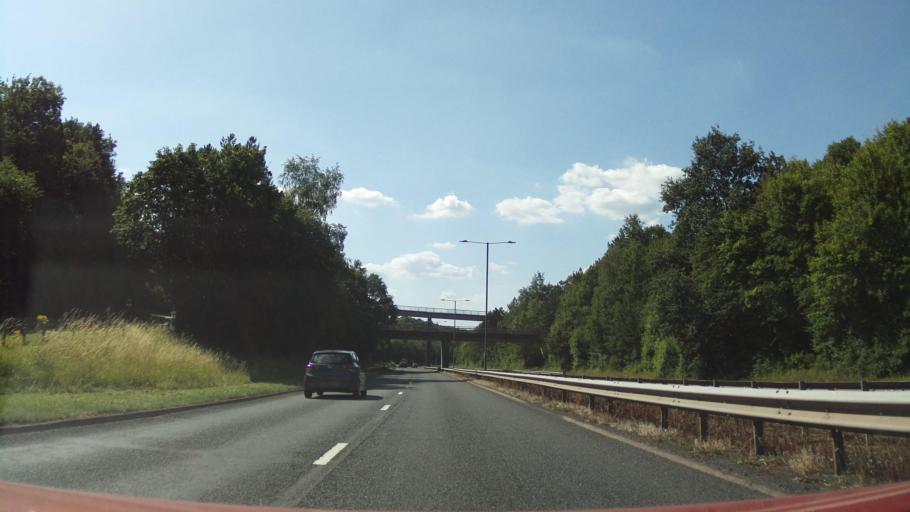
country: GB
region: England
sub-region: Worcestershire
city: Redditch
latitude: 52.2976
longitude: -1.9544
